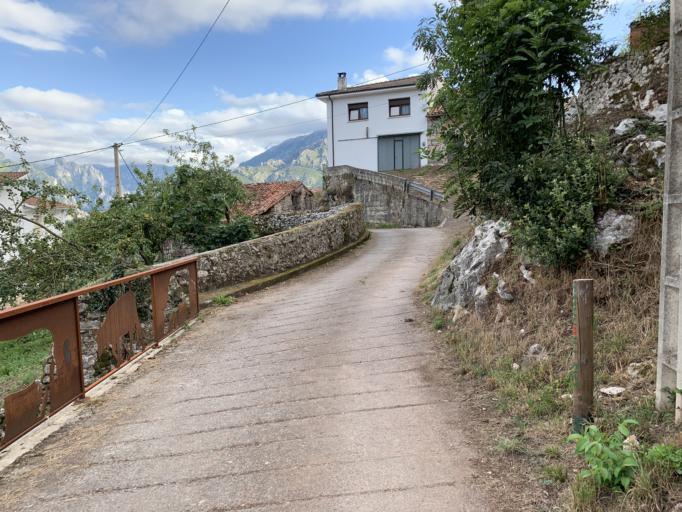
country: ES
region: Asturias
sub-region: Province of Asturias
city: Carrena
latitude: 43.3259
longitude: -4.8640
